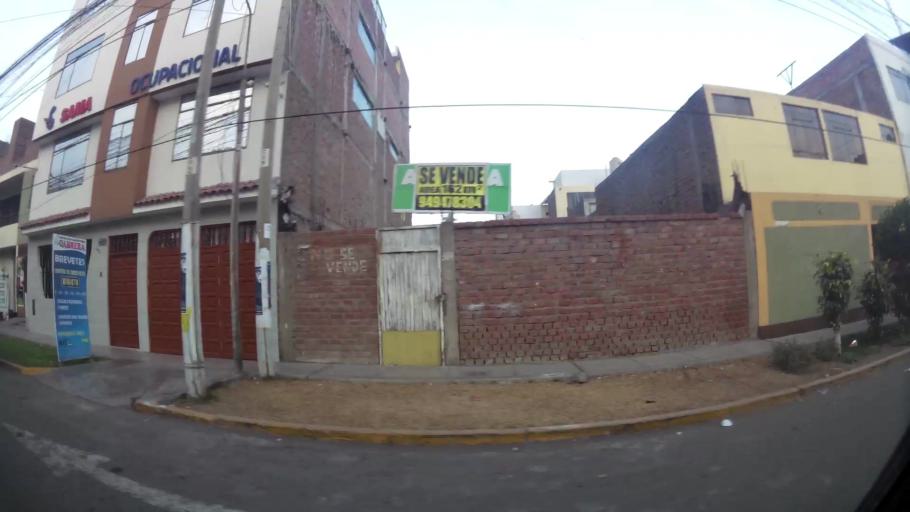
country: PE
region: La Libertad
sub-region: Provincia de Trujillo
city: Trujillo
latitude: -8.0993
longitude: -79.0357
